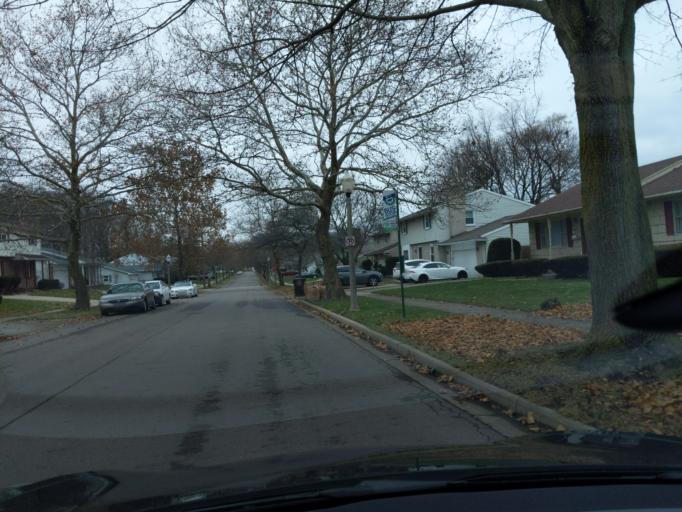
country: US
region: Michigan
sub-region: Ingham County
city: Lansing
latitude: 42.7053
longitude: -84.5861
